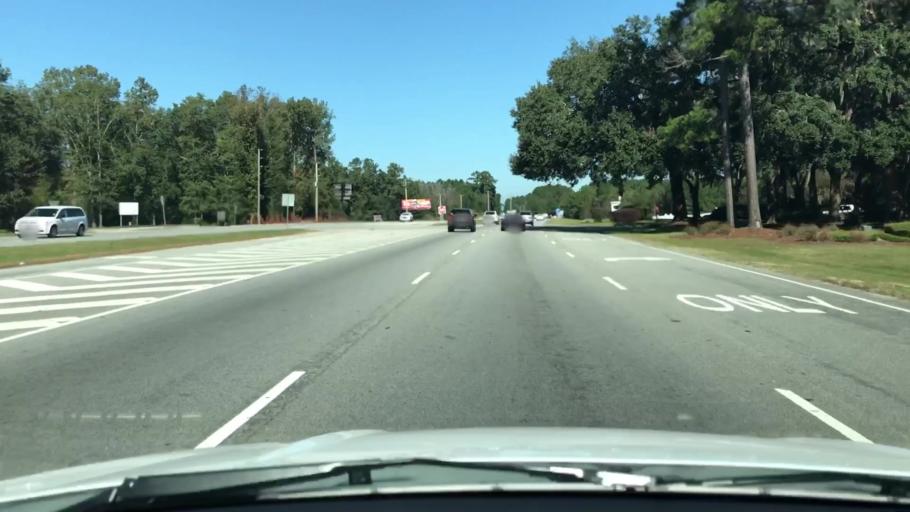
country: US
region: South Carolina
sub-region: Beaufort County
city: Bluffton
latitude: 32.3459
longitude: -80.9267
